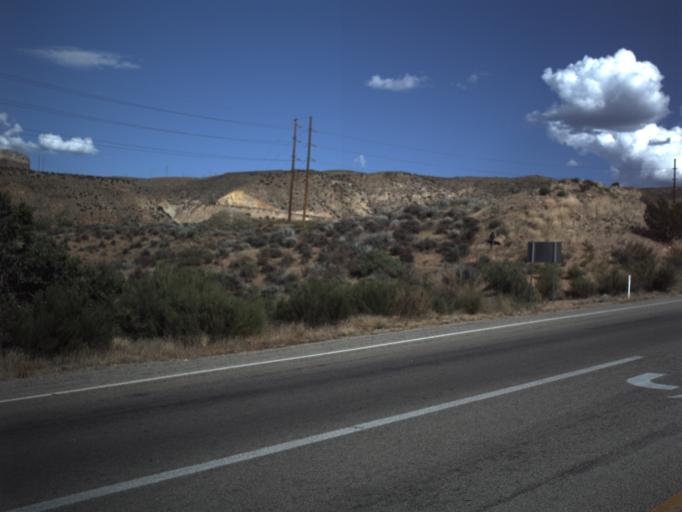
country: US
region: Utah
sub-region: Washington County
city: LaVerkin
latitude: 37.2179
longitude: -113.2744
